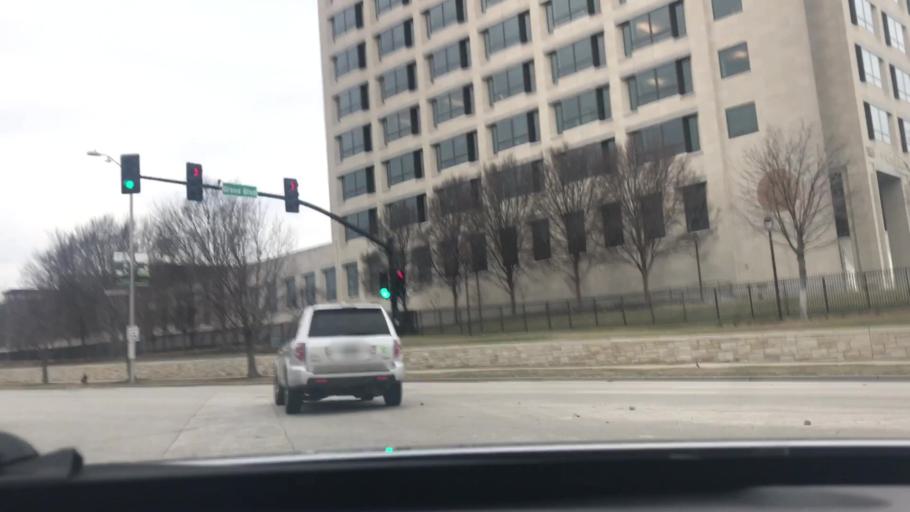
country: US
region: Missouri
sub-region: Jackson County
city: Kansas City
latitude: 39.0763
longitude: -94.5849
